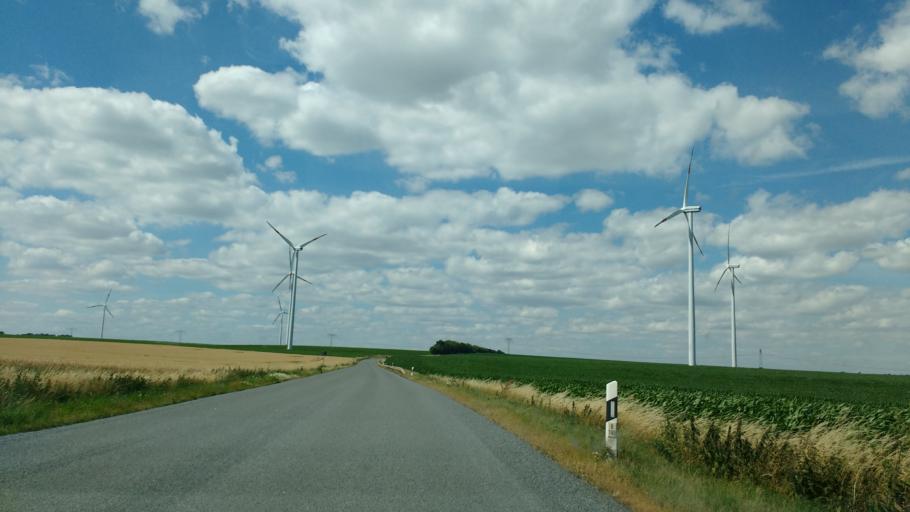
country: DE
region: Saxony-Anhalt
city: Querfurt
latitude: 51.4062
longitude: 11.5841
